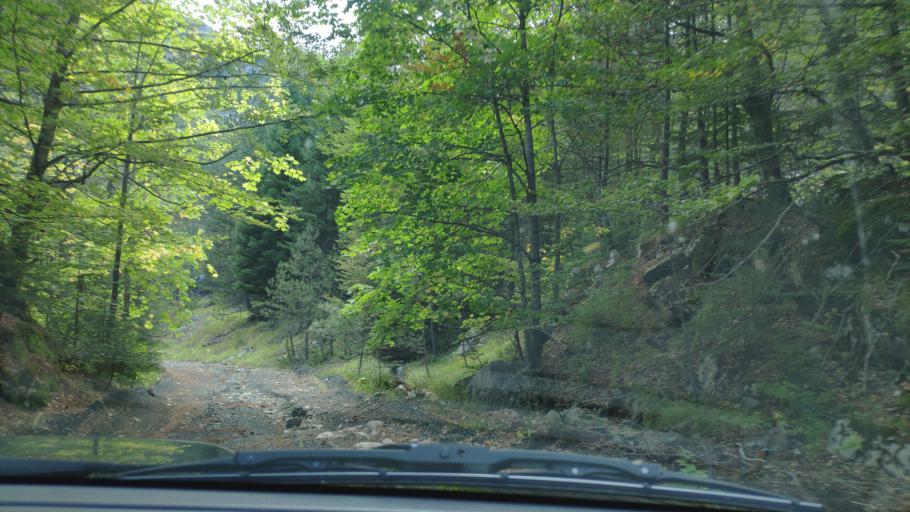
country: AL
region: Korce
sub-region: Rrethi i Devollit
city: Miras
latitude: 40.3412
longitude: 20.8978
